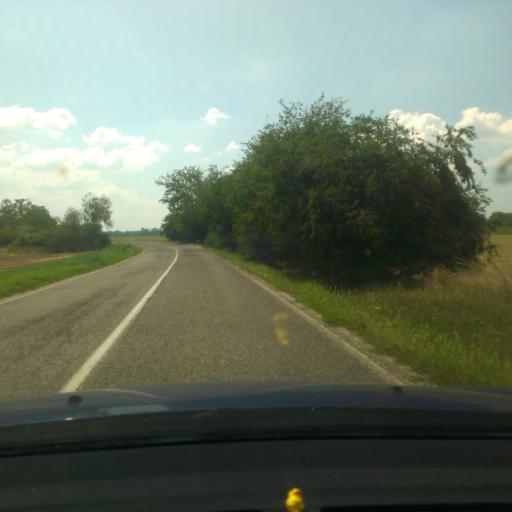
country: SK
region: Trnavsky
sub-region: Okres Trnava
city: Piestany
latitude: 48.5176
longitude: 17.8257
